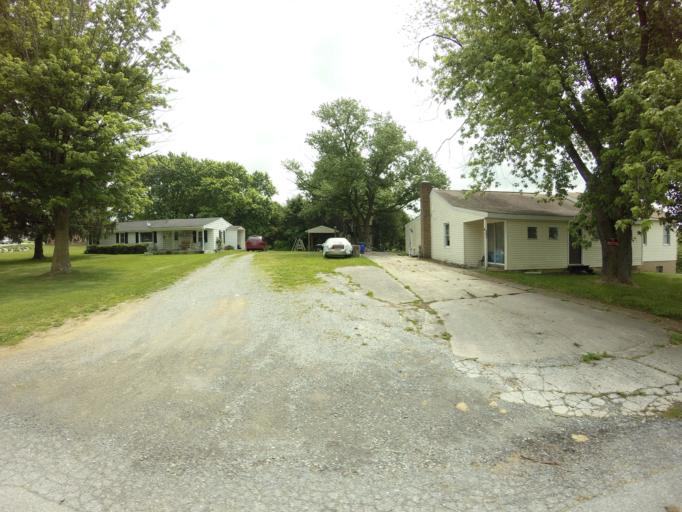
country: US
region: Maryland
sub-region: Frederick County
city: Brunswick
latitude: 39.3180
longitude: -77.6214
